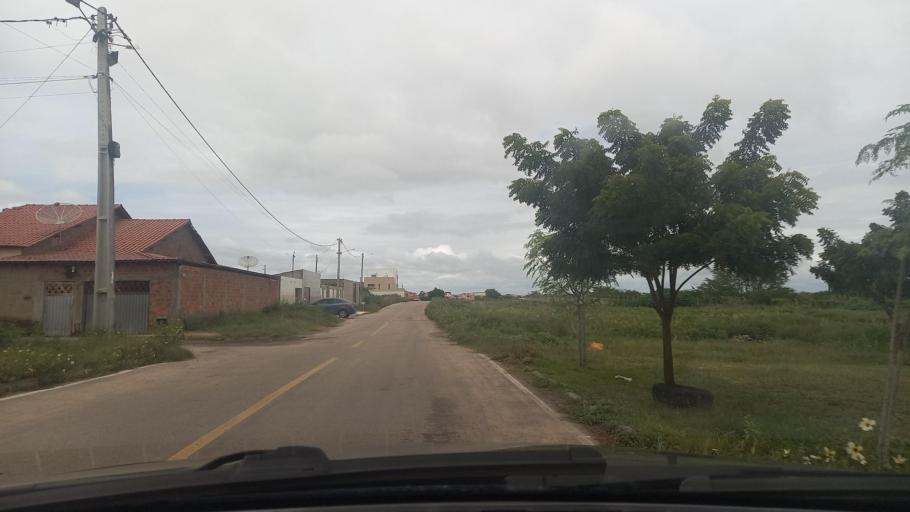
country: BR
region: Bahia
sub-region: Paulo Afonso
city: Paulo Afonso
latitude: -9.4022
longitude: -38.2438
